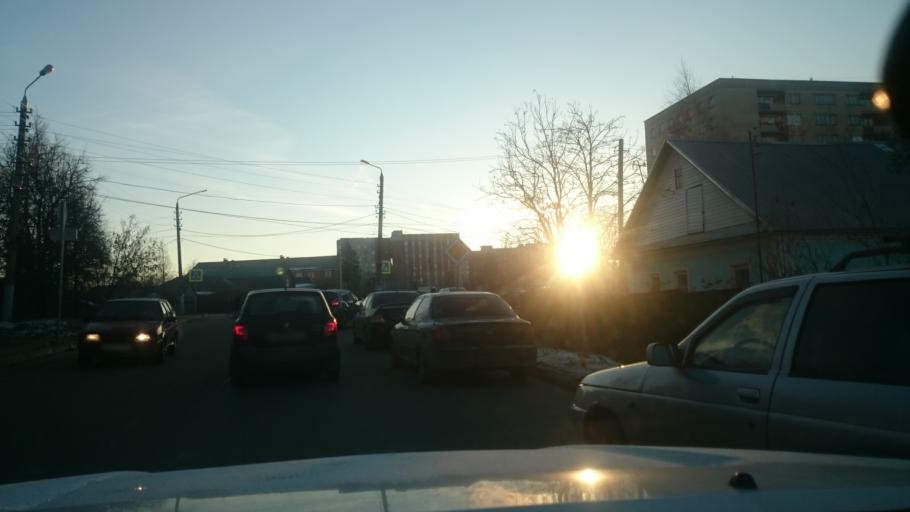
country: RU
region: Tula
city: Tula
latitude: 54.2073
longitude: 37.6971
